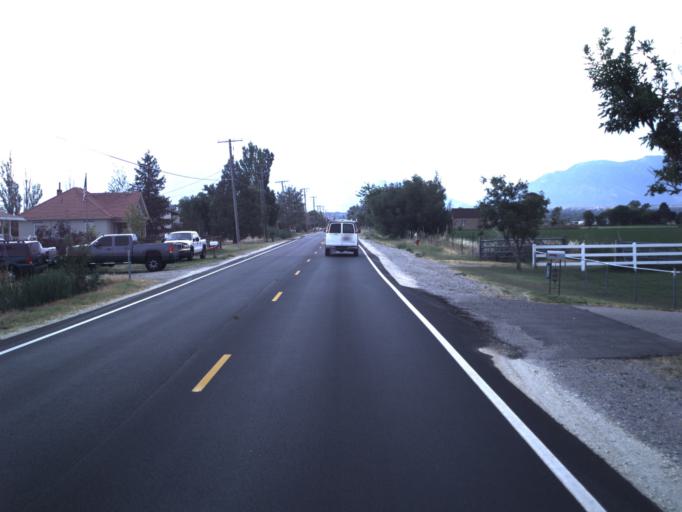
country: US
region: Utah
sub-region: Weber County
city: Hooper
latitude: 41.1639
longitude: -112.1085
